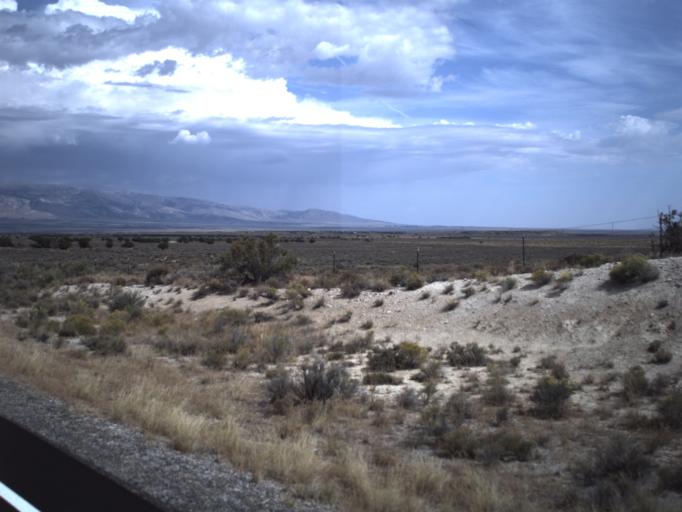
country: US
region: Idaho
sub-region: Cassia County
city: Burley
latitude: 41.7072
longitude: -113.5313
